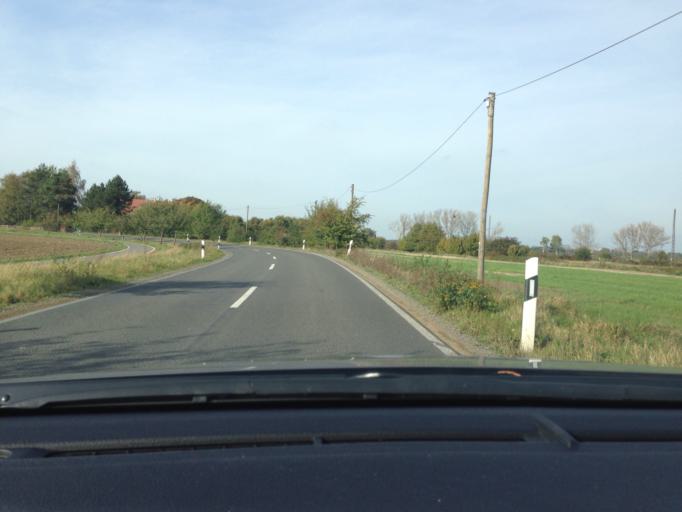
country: DE
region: Saxony
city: Borsdorf
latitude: 51.3330
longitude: 12.5622
